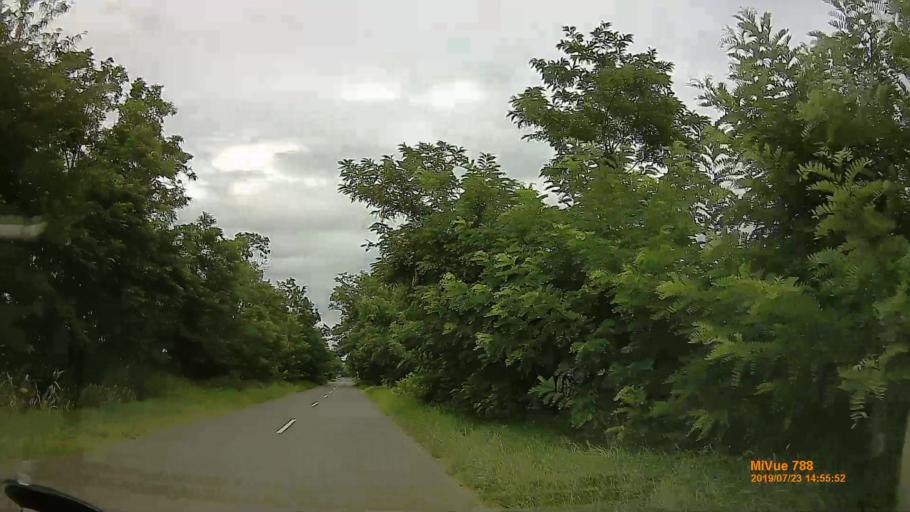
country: HU
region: Szabolcs-Szatmar-Bereg
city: Kalmanhaza
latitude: 47.8946
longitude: 21.6617
